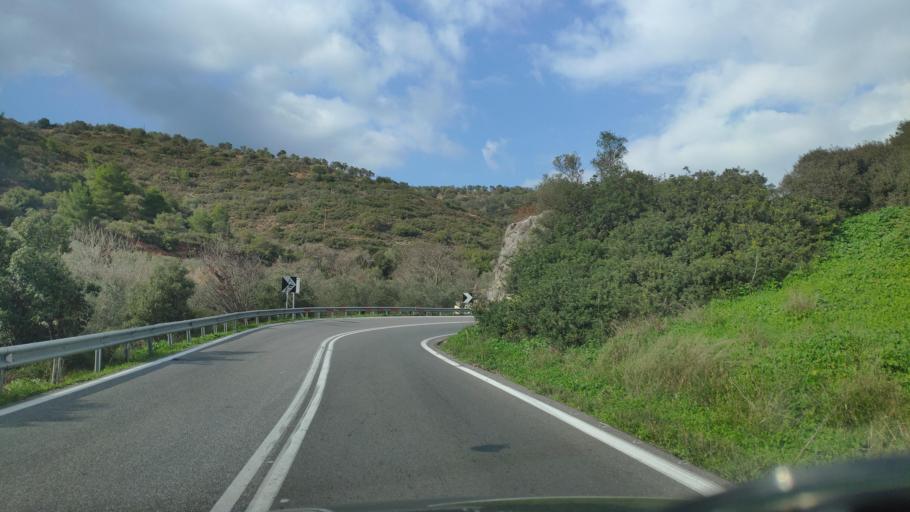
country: GR
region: Peloponnese
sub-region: Nomos Korinthias
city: Ayios Vasilios
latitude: 37.7713
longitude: 22.7256
